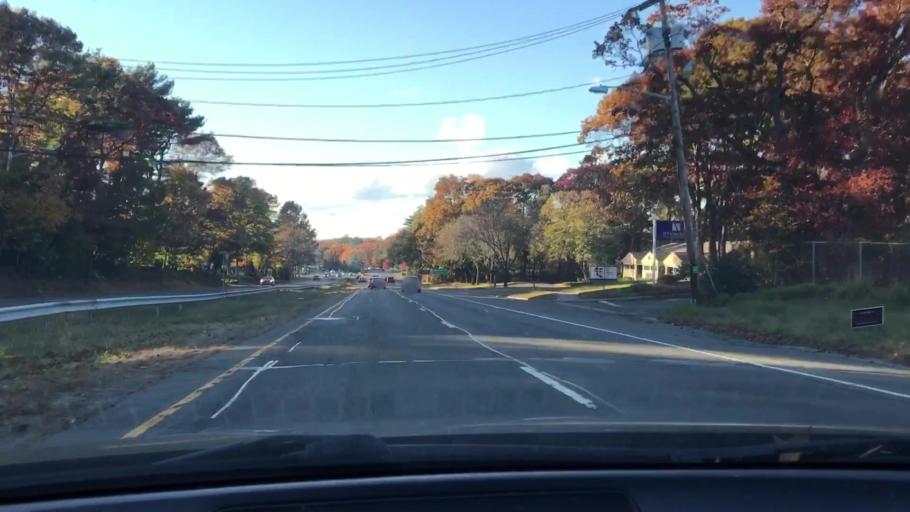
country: US
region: New York
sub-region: Suffolk County
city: Hauppauge
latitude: 40.8212
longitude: -73.2049
